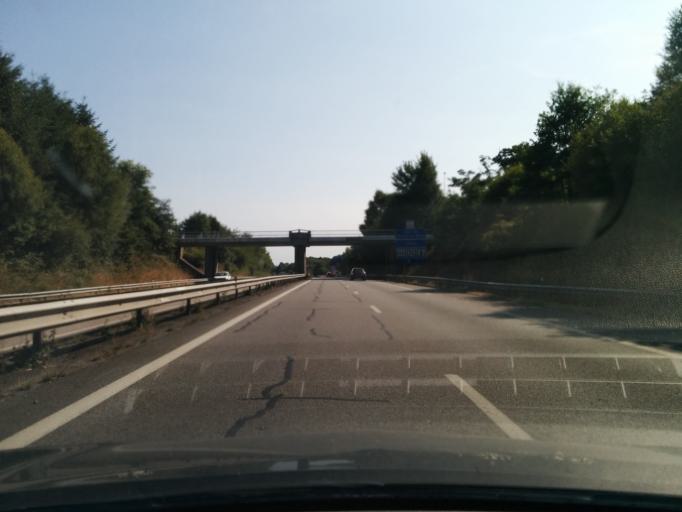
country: FR
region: Limousin
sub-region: Departement de la Haute-Vienne
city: Rilhac-Rancon
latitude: 45.9174
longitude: 1.2961
